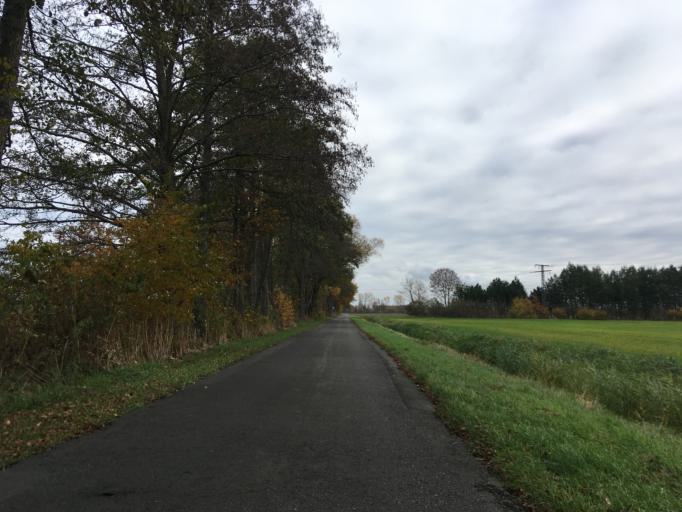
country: DE
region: Brandenburg
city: Drehnow
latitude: 51.8622
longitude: 14.3520
